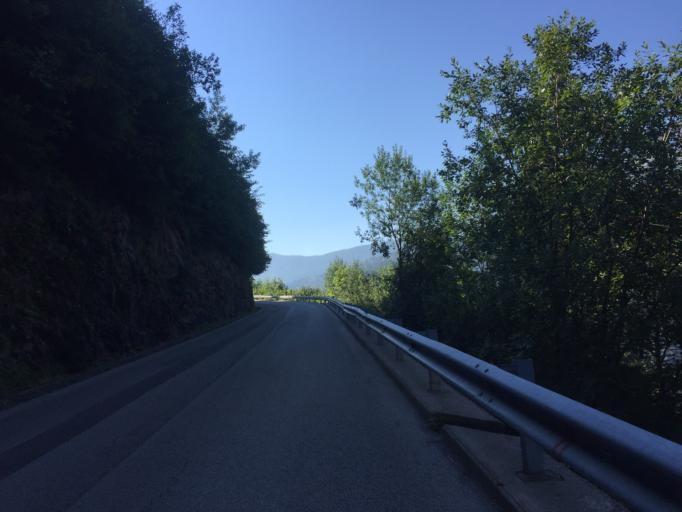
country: IT
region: Friuli Venezia Giulia
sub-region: Provincia di Udine
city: Forni Avoltri
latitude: 46.5775
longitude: 12.8043
